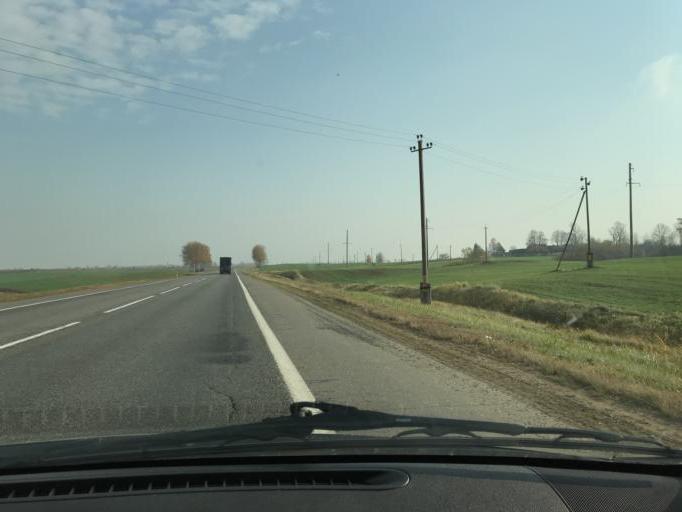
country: BY
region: Vitebsk
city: Chashniki
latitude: 55.0134
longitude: 29.1040
